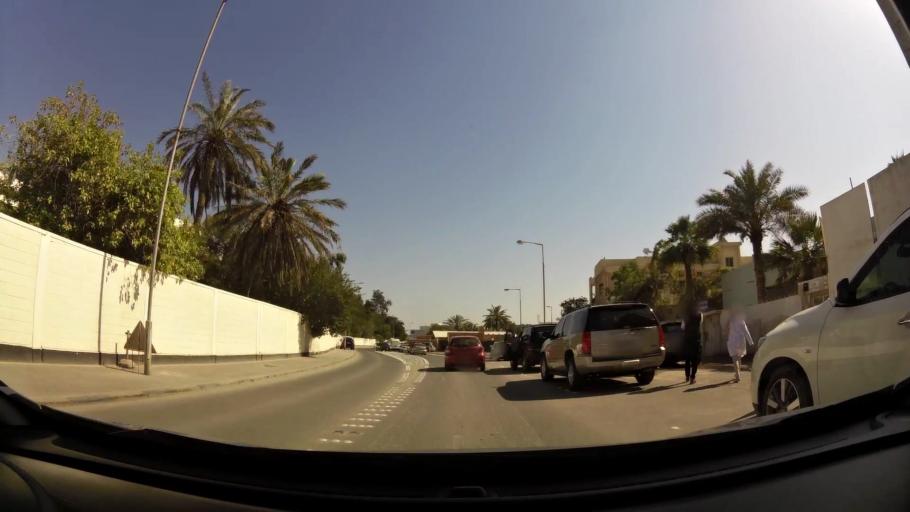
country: BH
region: Manama
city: Manama
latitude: 26.2163
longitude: 50.5700
